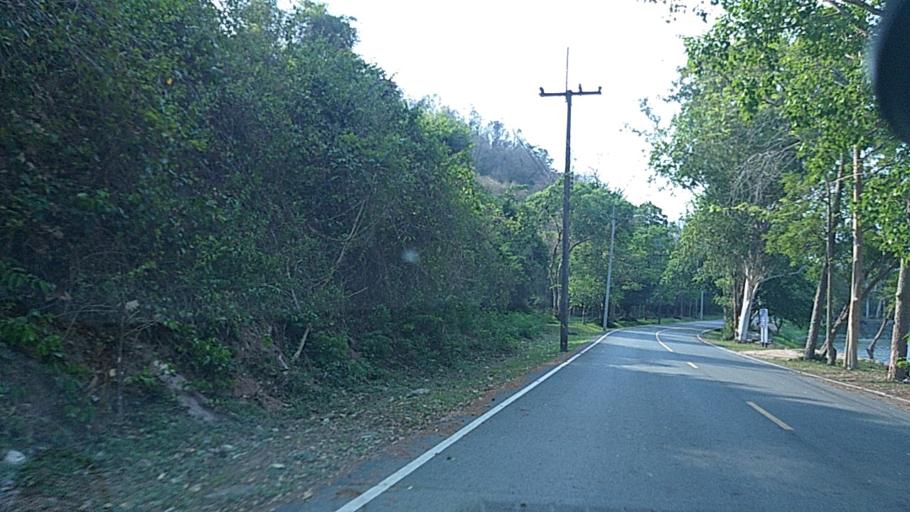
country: TH
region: Sara Buri
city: Saraburi
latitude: 14.4424
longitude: 100.9586
